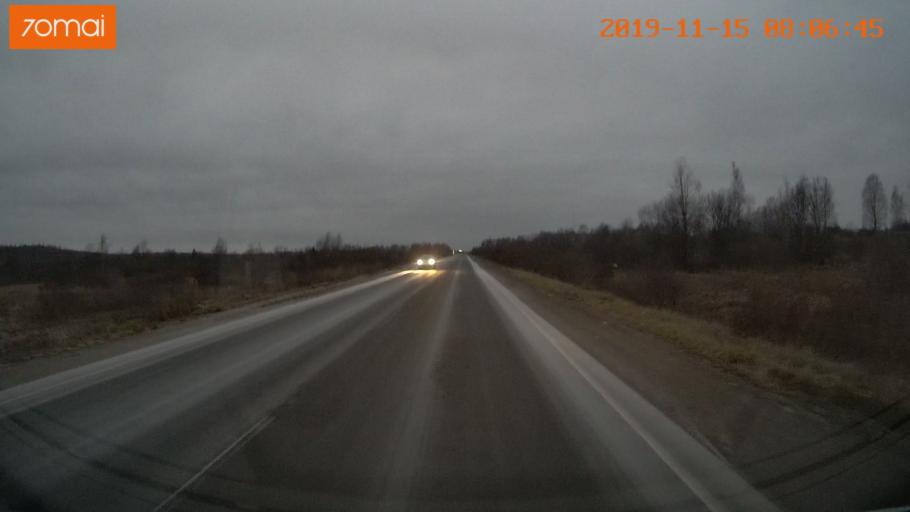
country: RU
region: Vologda
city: Cherepovets
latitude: 59.0233
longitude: 38.0327
